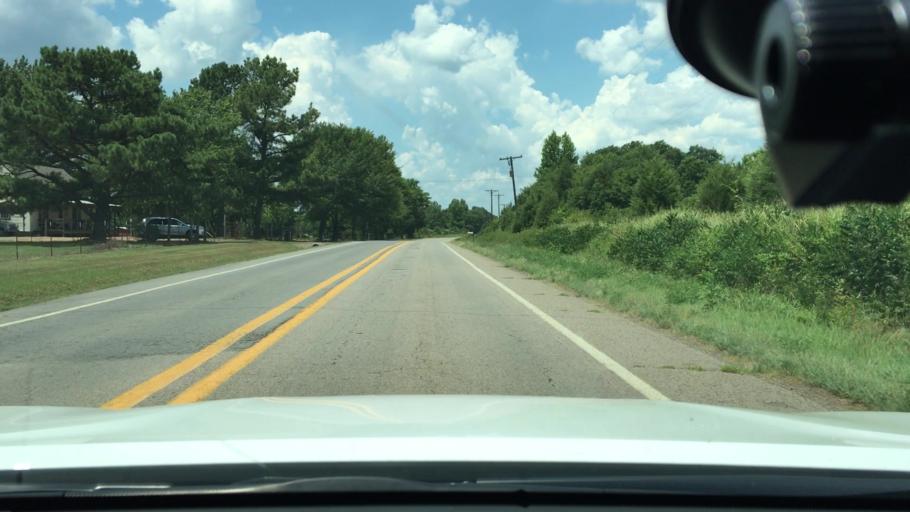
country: US
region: Arkansas
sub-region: Logan County
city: Booneville
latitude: 35.1476
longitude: -93.8394
